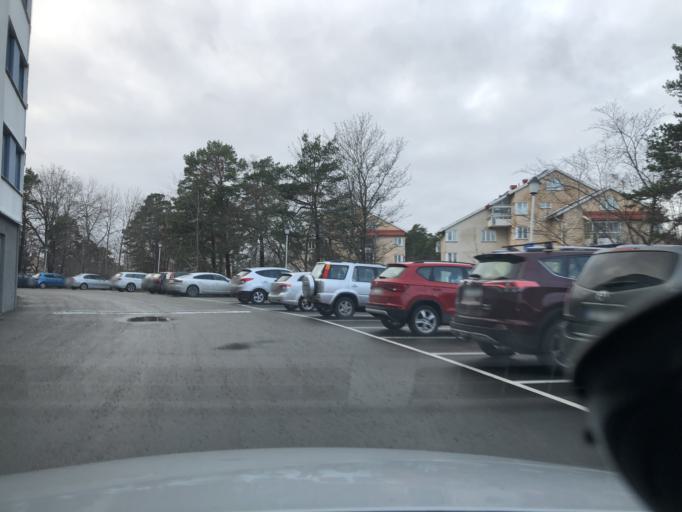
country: SE
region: Stockholm
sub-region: Stockholms Kommun
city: Arsta
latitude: 59.3003
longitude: 18.0600
